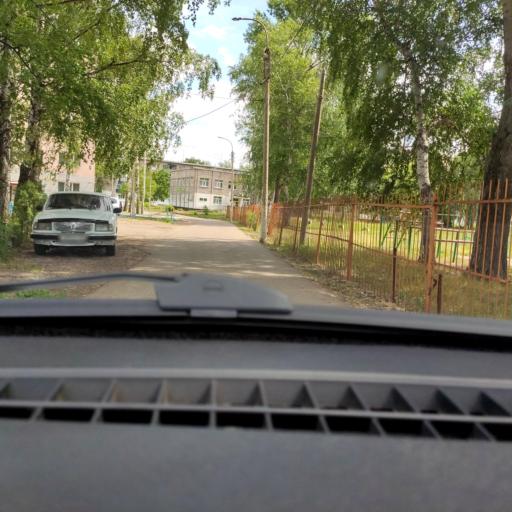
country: RU
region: Bashkortostan
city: Sterlitamak
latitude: 53.6362
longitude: 55.9297
